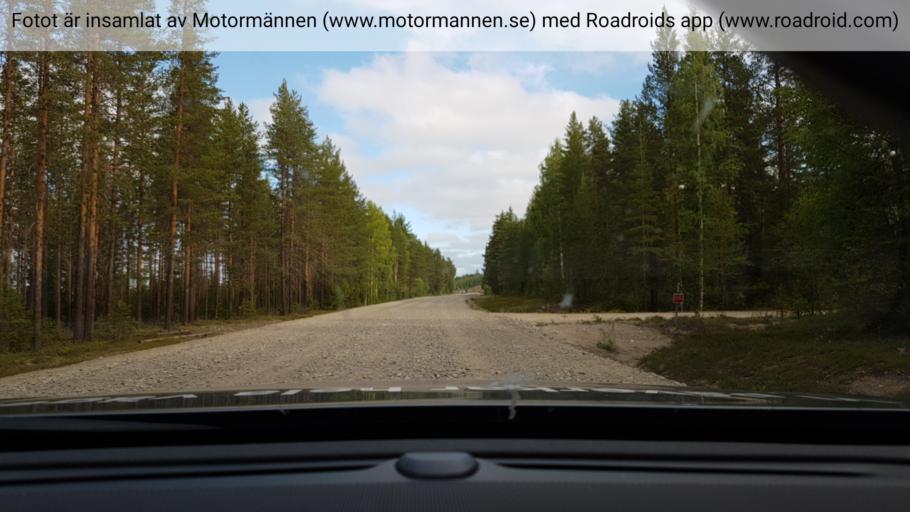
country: SE
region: Vaesterbotten
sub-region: Norsjo Kommun
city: Norsjoe
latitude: 64.6148
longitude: 19.2902
